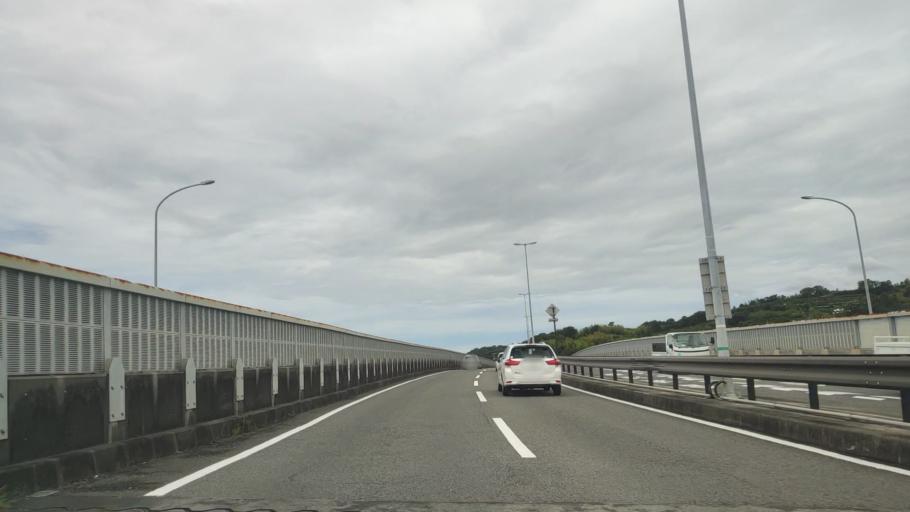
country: JP
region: Wakayama
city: Tanabe
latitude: 33.7418
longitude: 135.3876
